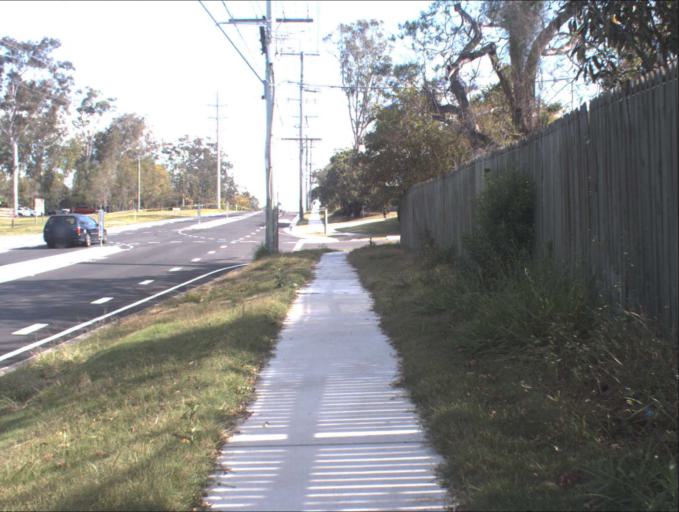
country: AU
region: Queensland
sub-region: Logan
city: Slacks Creek
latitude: -27.6483
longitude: 153.1358
